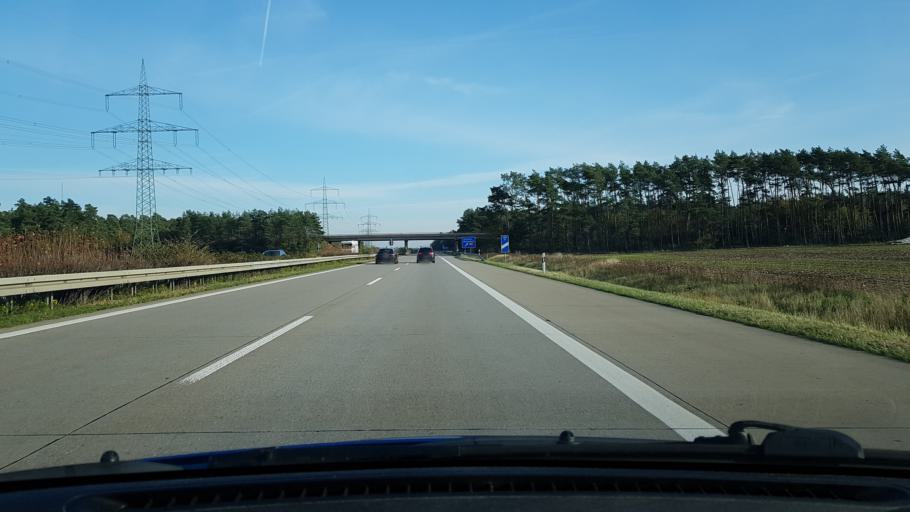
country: DE
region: Mecklenburg-Vorpommern
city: Zarrentin
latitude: 53.5113
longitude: 10.8903
